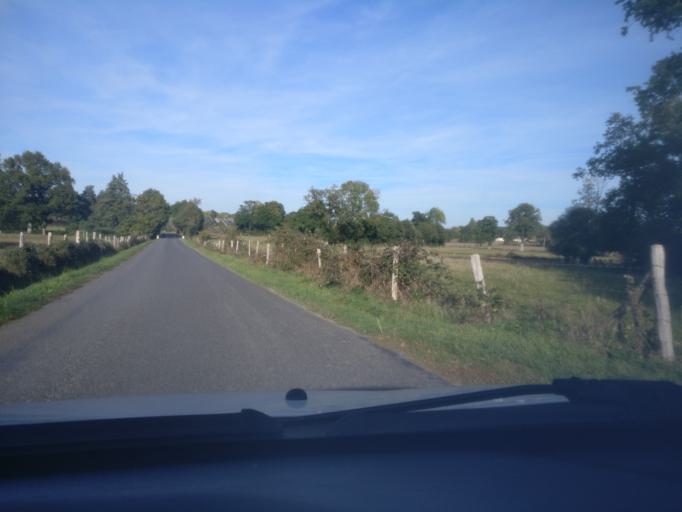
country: FR
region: Lower Normandy
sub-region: Departement de la Manche
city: Marcey-les-Greves
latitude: 48.6991
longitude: -1.4022
